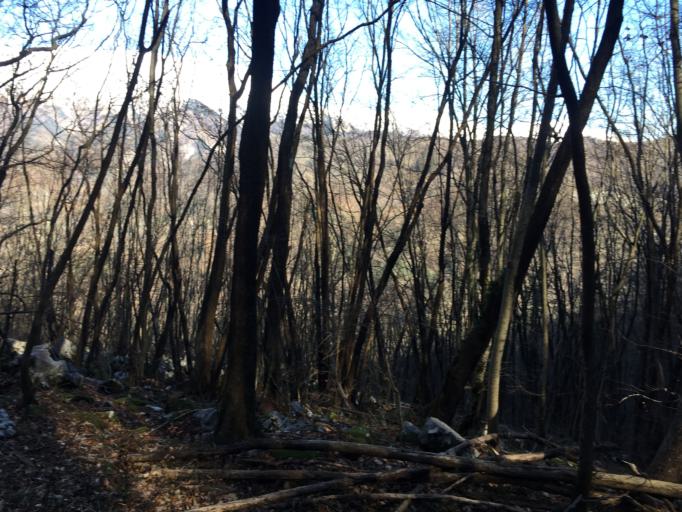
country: IT
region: Friuli Venezia Giulia
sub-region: Provincia di Udine
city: Taipana
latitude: 46.2461
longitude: 13.3180
